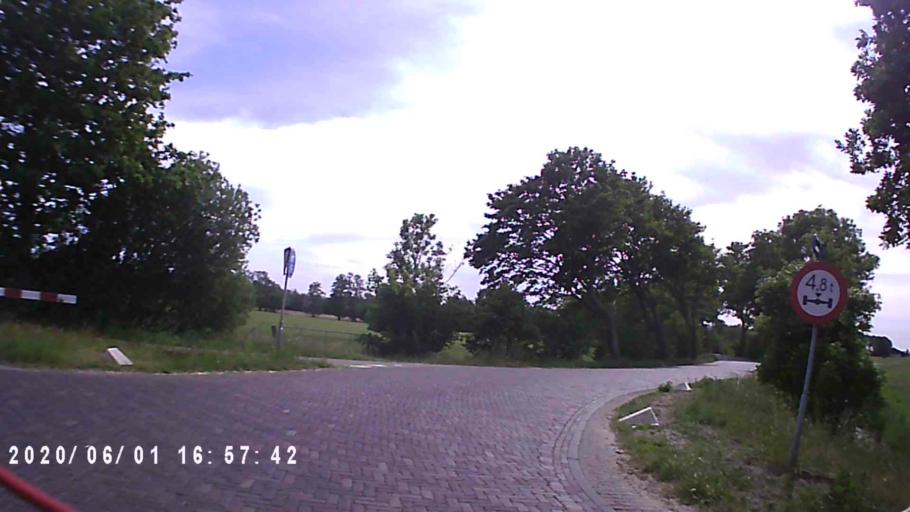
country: NL
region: Friesland
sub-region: Gemeente Tytsjerksteradiel
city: Hurdegaryp
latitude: 53.1911
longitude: 5.9294
